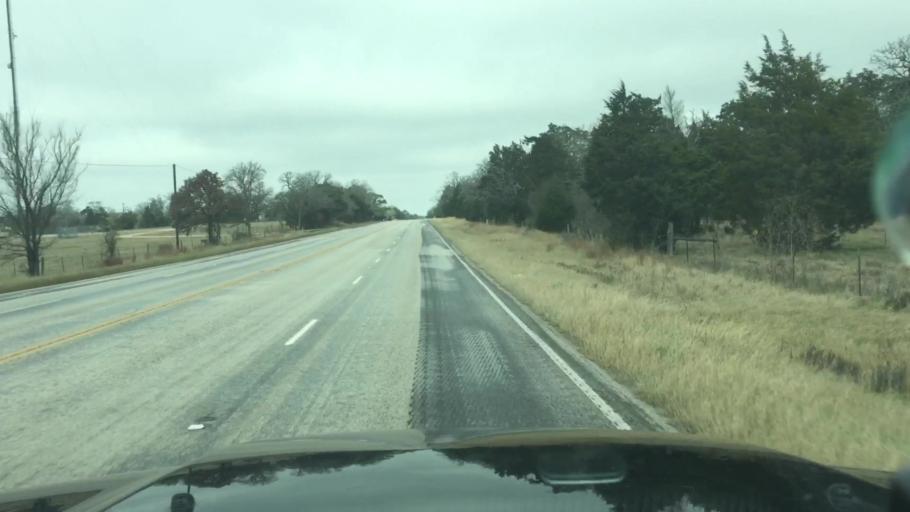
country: US
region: Texas
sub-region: Lee County
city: Giddings
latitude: 30.1073
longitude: -96.9146
